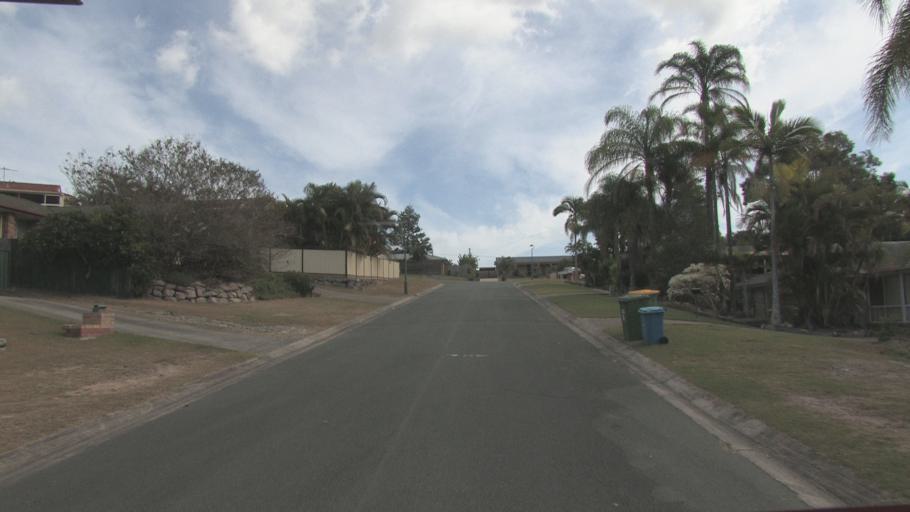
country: AU
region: Queensland
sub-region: Logan
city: Waterford West
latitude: -27.6983
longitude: 153.1590
